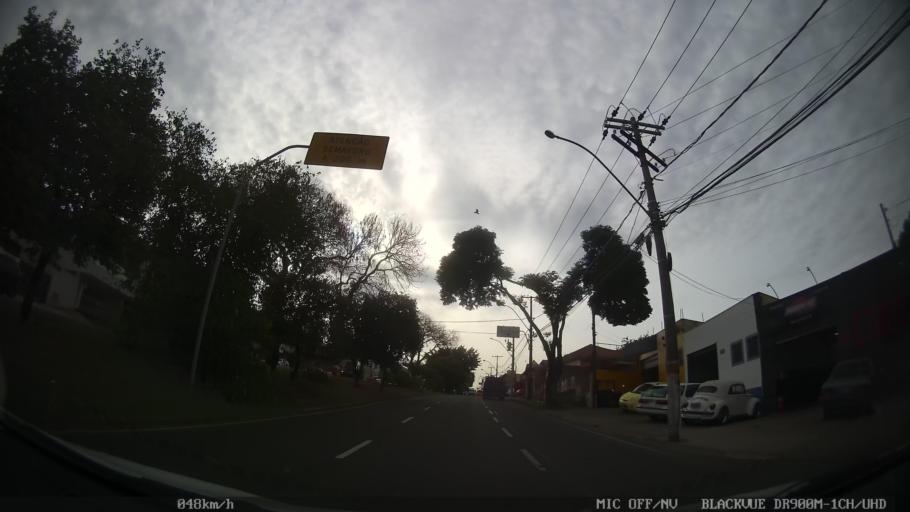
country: BR
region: Sao Paulo
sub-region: Piracicaba
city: Piracicaba
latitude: -22.7359
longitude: -47.6322
